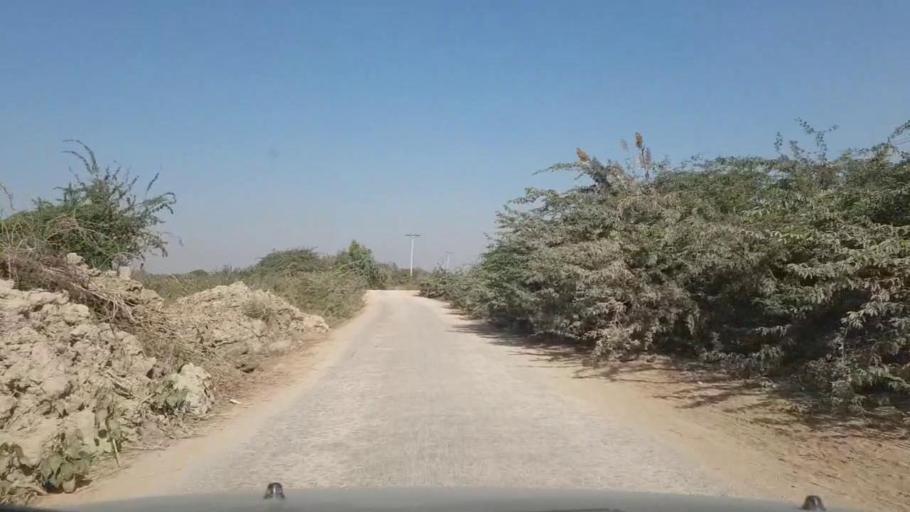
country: PK
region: Sindh
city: Thatta
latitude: 24.7950
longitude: 67.9018
